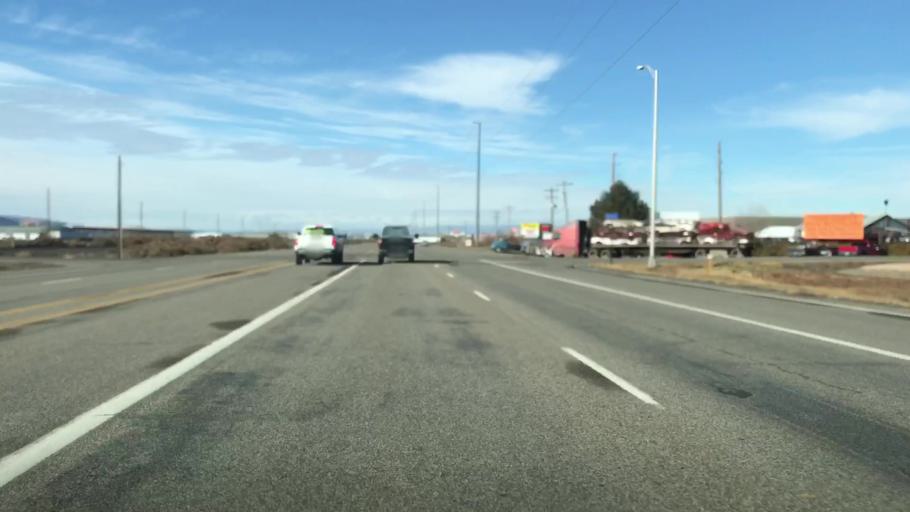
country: US
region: Colorado
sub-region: Mesa County
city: Redlands
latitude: 39.1057
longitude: -108.6362
